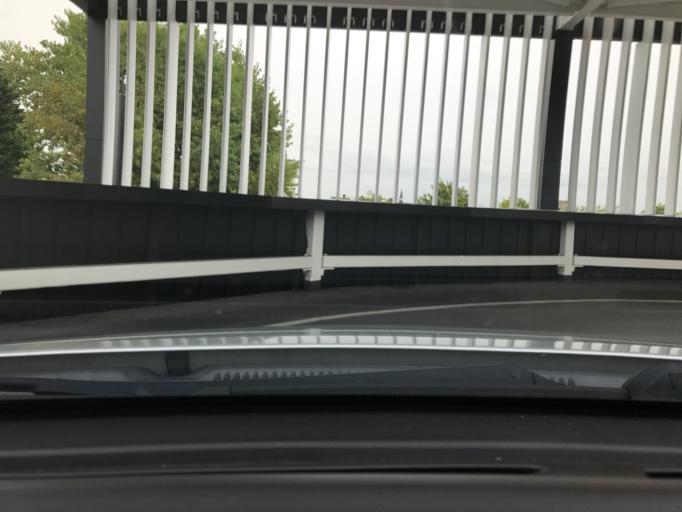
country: GB
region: England
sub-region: Cheshire West and Chester
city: Northwich
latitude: 53.2640
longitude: -2.5113
